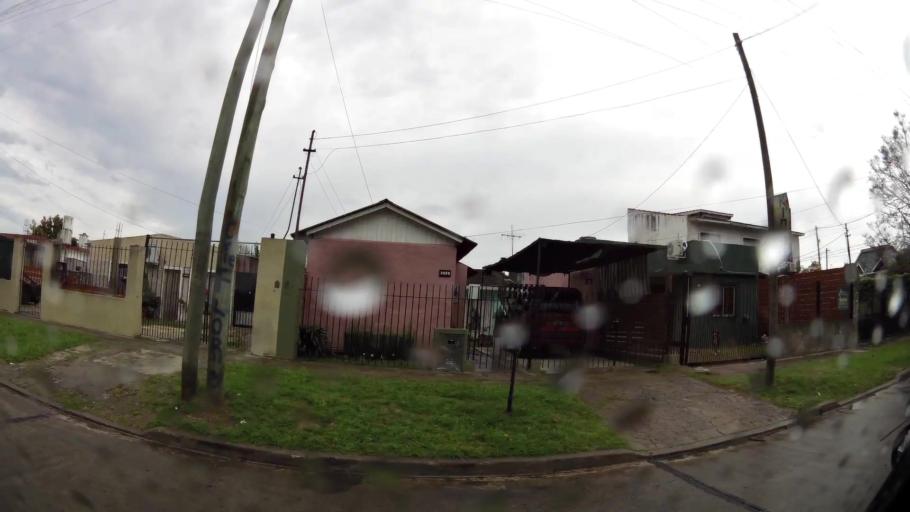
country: AR
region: Buenos Aires
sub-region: Partido de Quilmes
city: Quilmes
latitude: -34.7641
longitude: -58.2244
